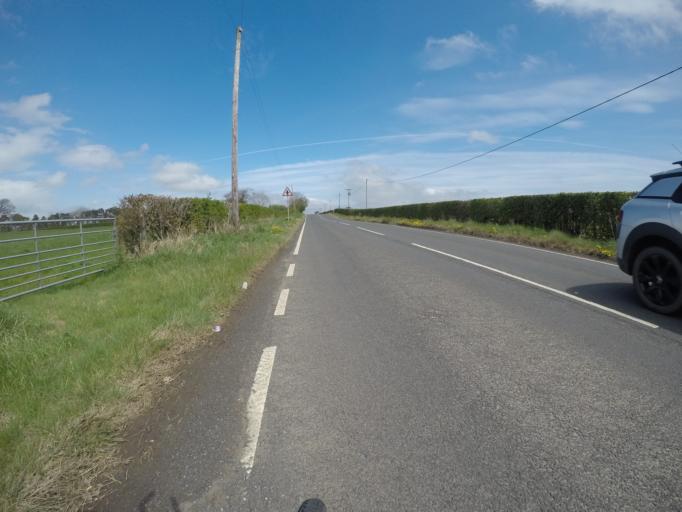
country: GB
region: Scotland
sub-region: East Ayrshire
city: Kilmaurs
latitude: 55.6610
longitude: -4.5492
